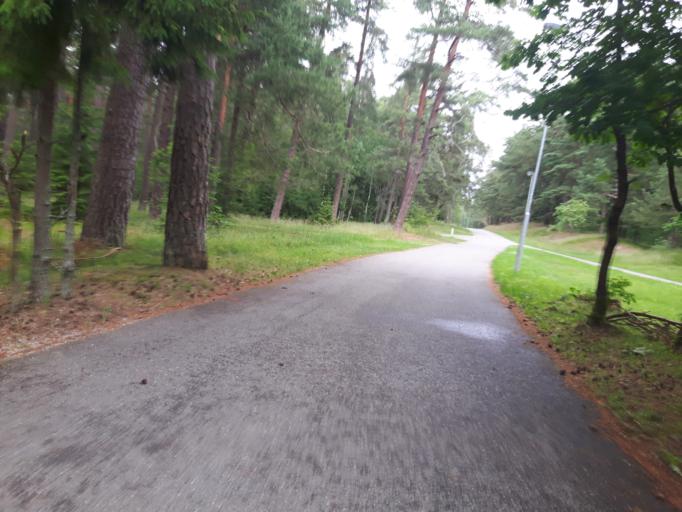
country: LT
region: Klaipedos apskritis
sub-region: Klaipeda
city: Klaipeda
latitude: 55.7439
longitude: 21.1221
